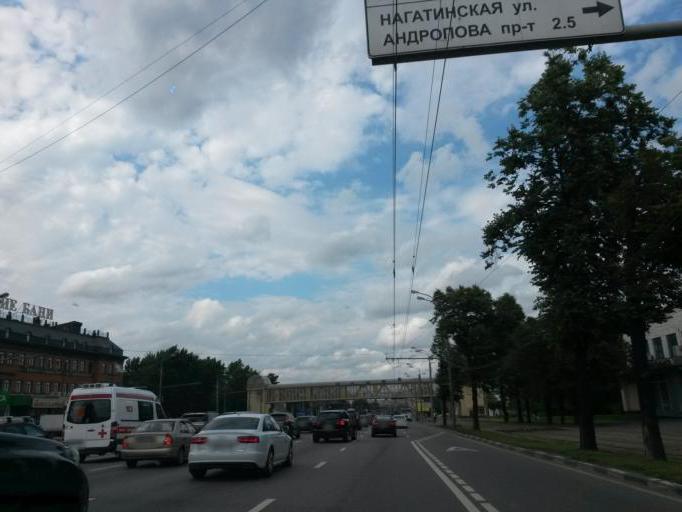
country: RU
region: Moscow
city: Kotlovka
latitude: 55.6797
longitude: 37.6249
